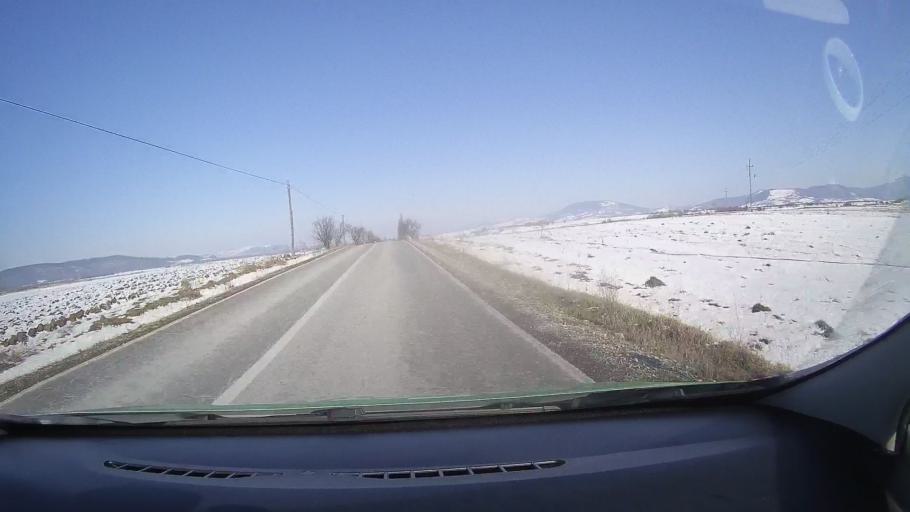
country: RO
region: Brasov
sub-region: Comuna Parau
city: Parau
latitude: 45.8571
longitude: 25.1965
